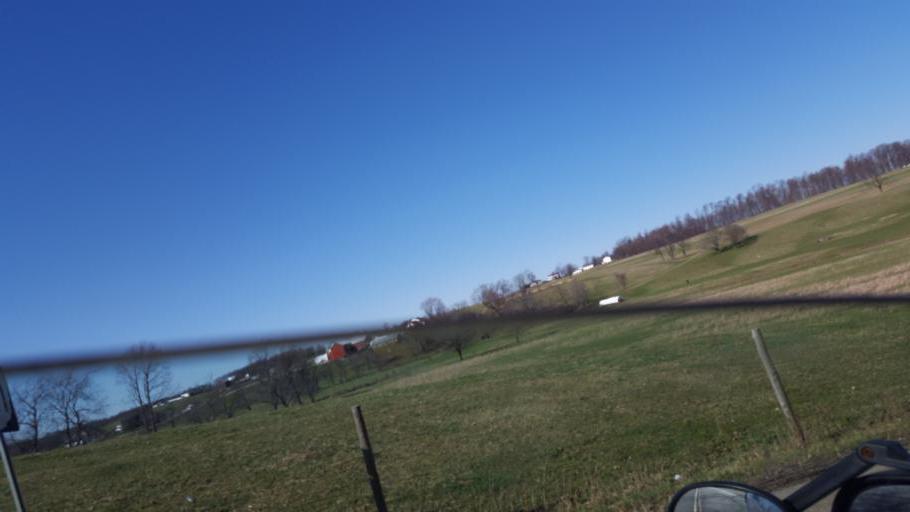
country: US
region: Ohio
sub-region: Wayne County
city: Apple Creek
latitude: 40.6673
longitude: -81.7412
